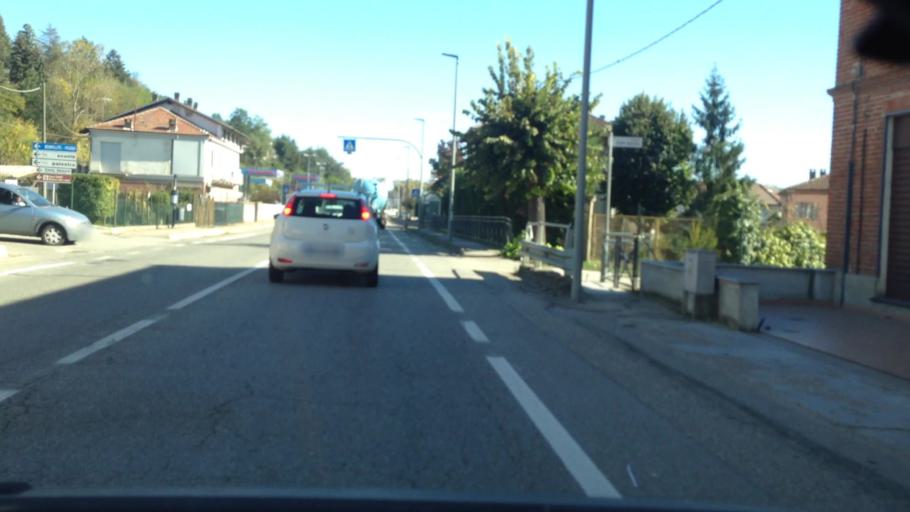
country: IT
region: Piedmont
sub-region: Provincia di Asti
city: Castello di Annone
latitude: 44.8775
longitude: 8.3200
